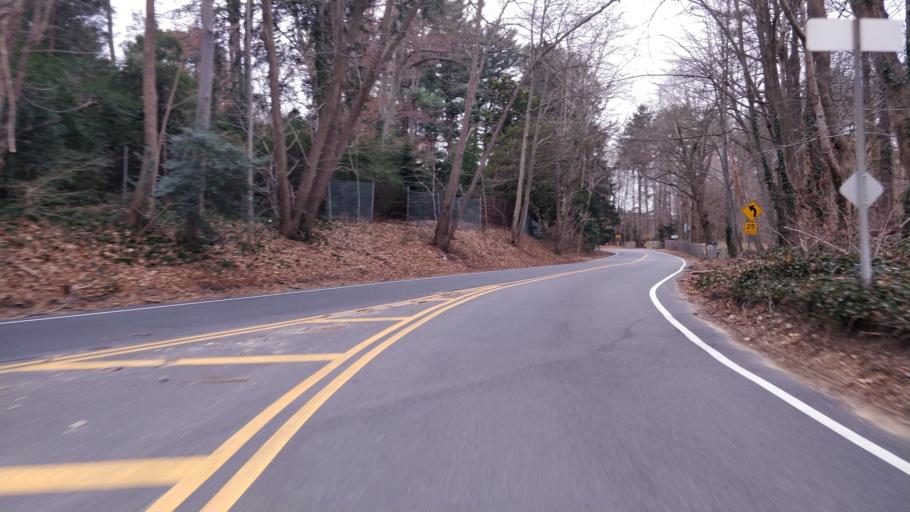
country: US
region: New York
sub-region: Nassau County
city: Old Westbury
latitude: 40.7808
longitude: -73.5906
